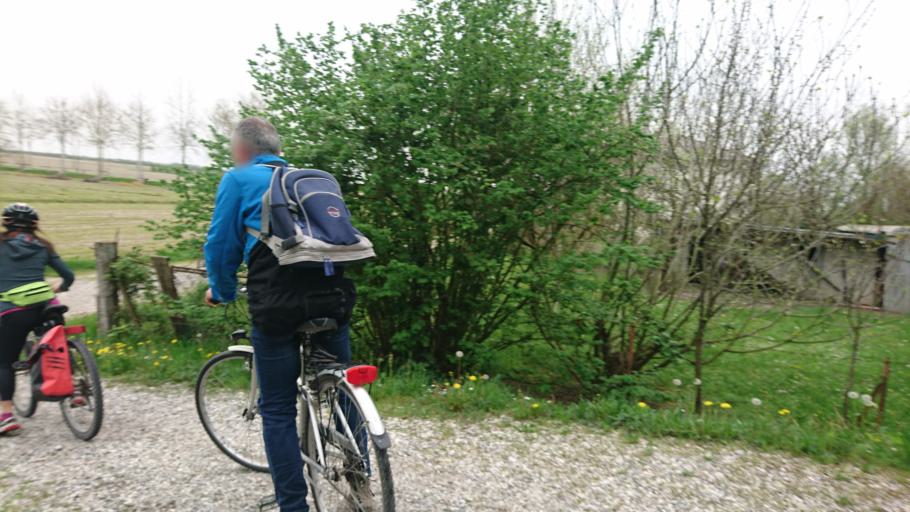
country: IT
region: Veneto
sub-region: Provincia di Venezia
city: Lugugnana
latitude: 45.6714
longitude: 12.9651
